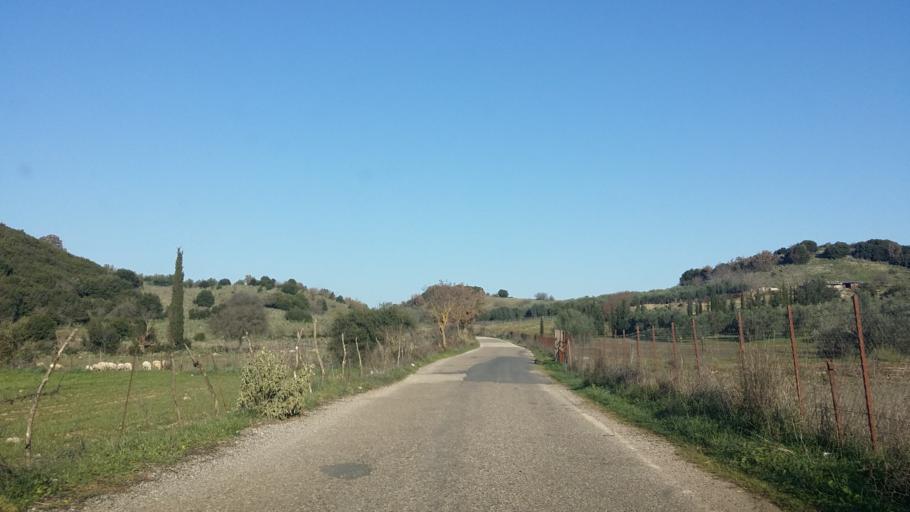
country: GR
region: West Greece
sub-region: Nomos Aitolias kai Akarnanias
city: Katouna
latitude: 38.7910
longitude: 21.1055
